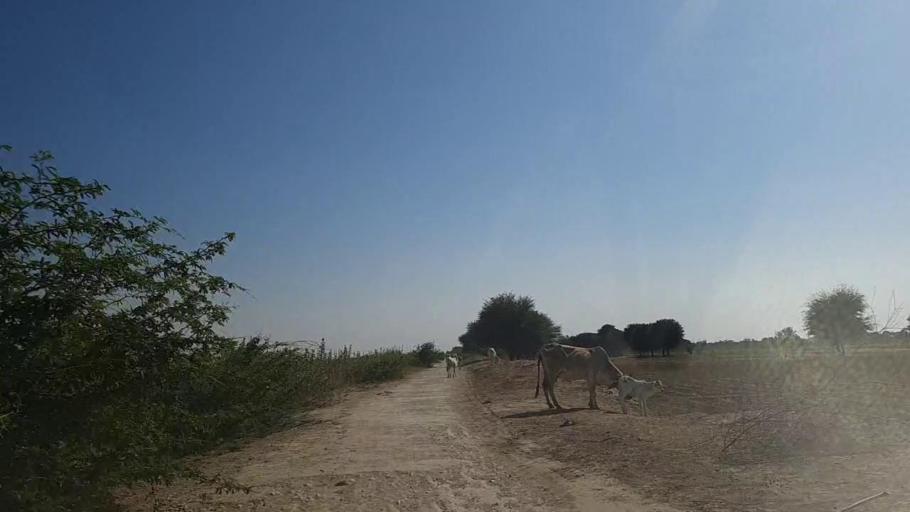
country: PK
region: Sindh
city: Samaro
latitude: 25.2406
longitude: 69.4838
